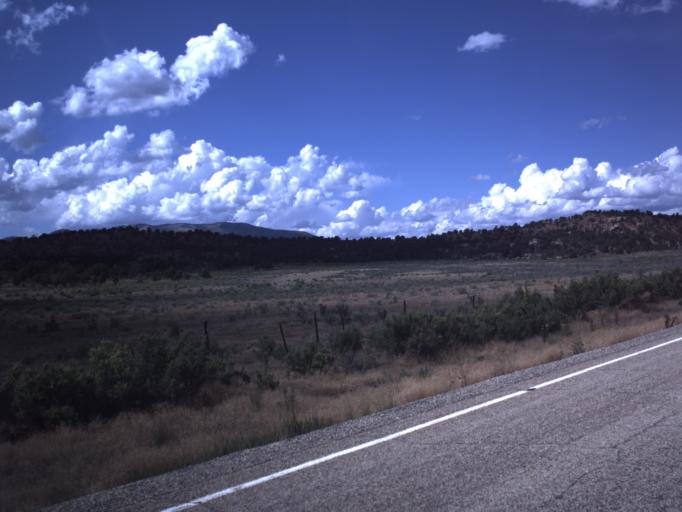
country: US
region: Utah
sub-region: Duchesne County
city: Duchesne
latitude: 40.2346
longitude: -110.7177
